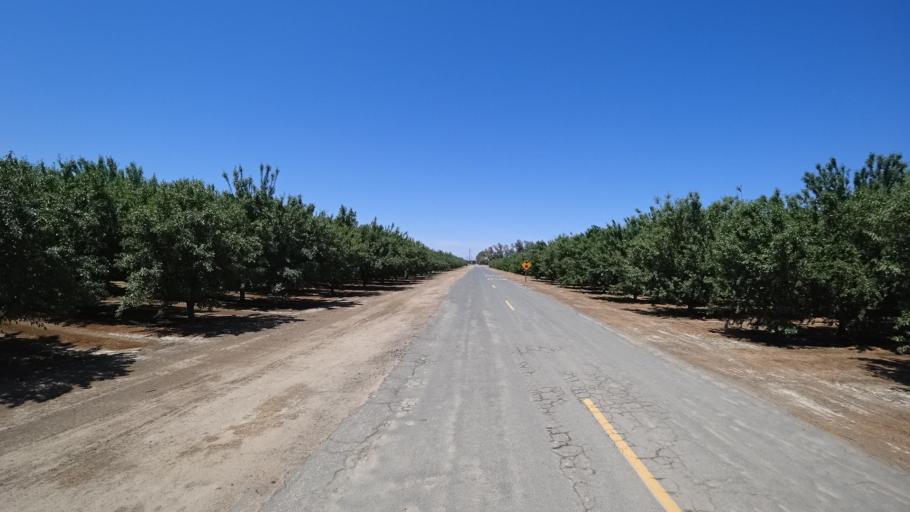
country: US
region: California
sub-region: Kings County
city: Lemoore
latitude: 36.3571
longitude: -119.8049
